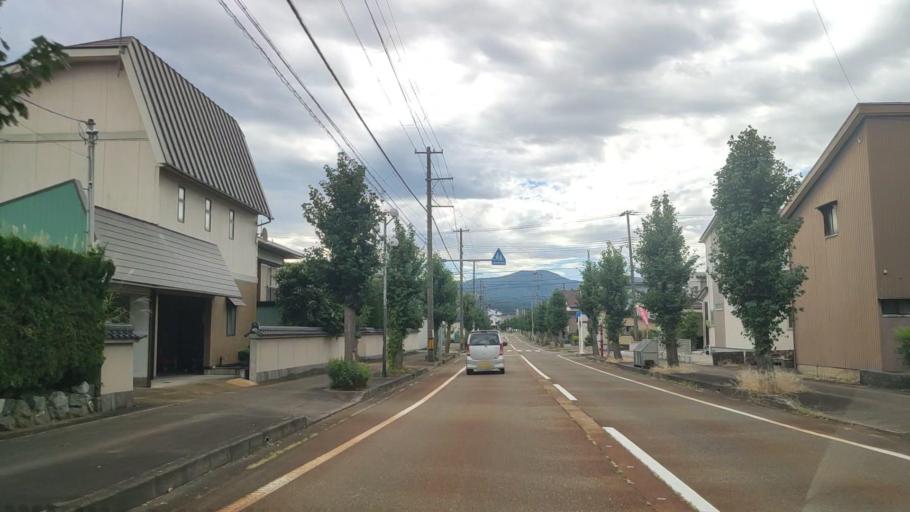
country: JP
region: Niigata
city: Arai
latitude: 37.0241
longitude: 138.2462
